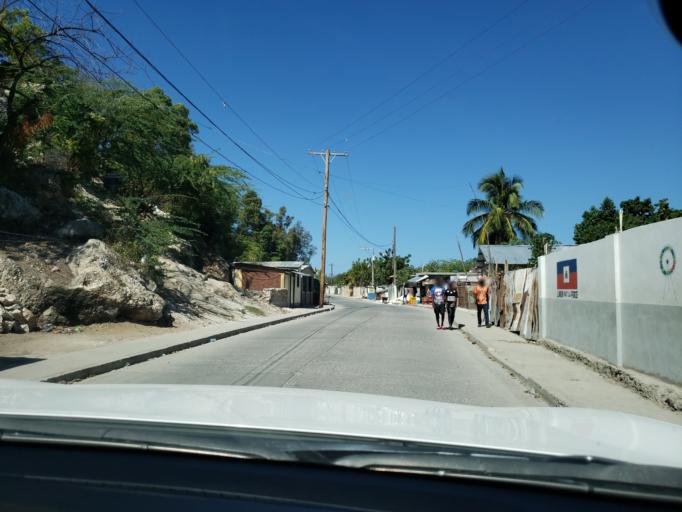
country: HT
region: Nippes
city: Miragoane
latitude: 18.4434
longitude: -73.0982
